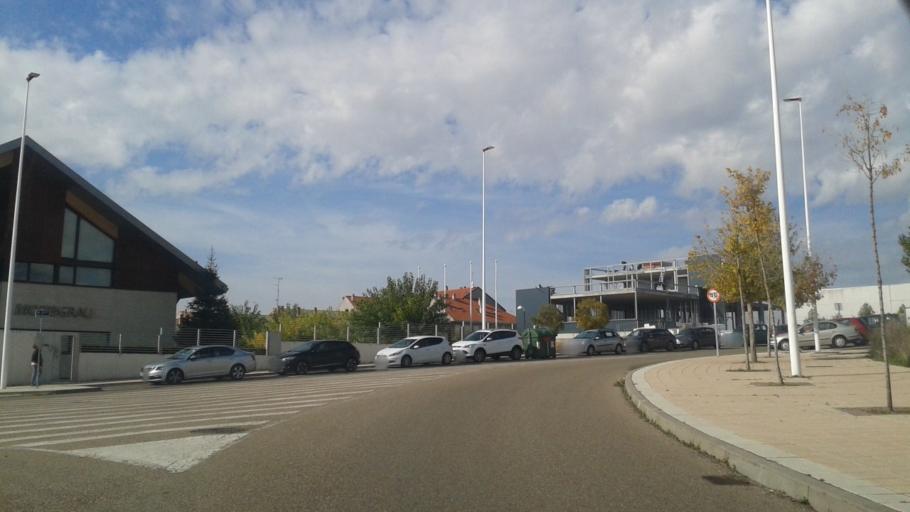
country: ES
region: Castille and Leon
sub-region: Provincia de Valladolid
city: Arroyo
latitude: 41.6270
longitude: -4.7666
